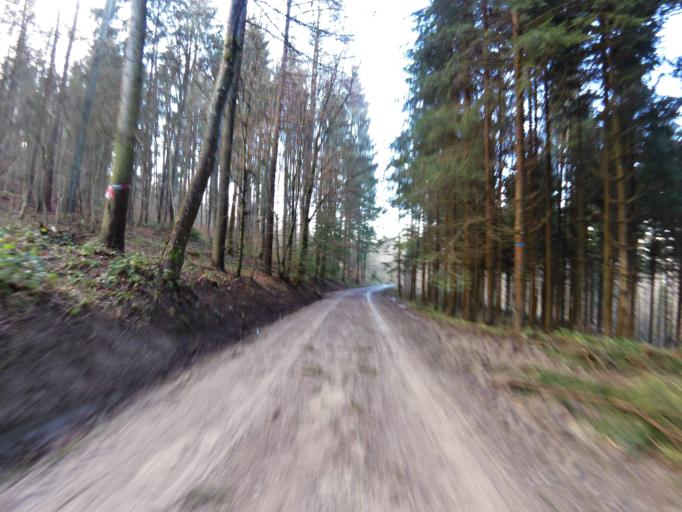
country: CH
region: Zurich
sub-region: Bezirk Dietikon
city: Uitikon
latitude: 47.3785
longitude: 8.4612
